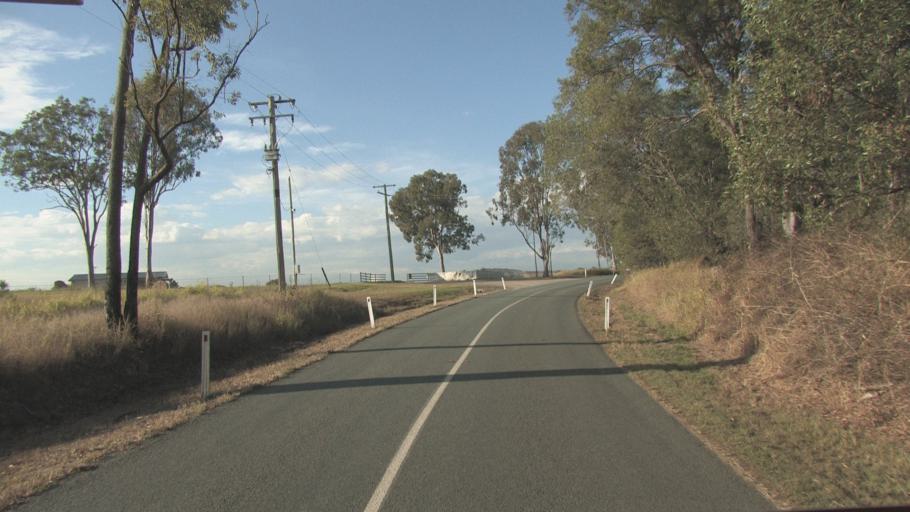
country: AU
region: Queensland
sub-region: Logan
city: Cedar Vale
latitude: -27.8526
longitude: 153.1234
